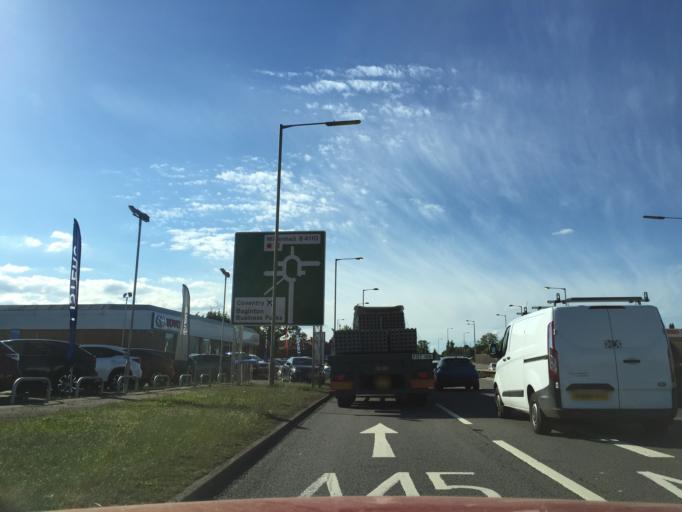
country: GB
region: England
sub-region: Warwickshire
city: Ryton on Dunsmore
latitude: 52.3765
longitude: -1.4629
